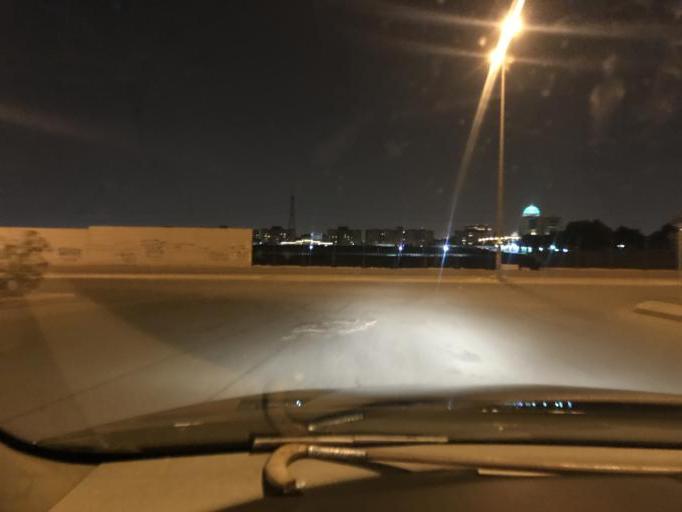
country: SA
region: Ar Riyad
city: Riyadh
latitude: 24.8157
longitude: 46.7164
